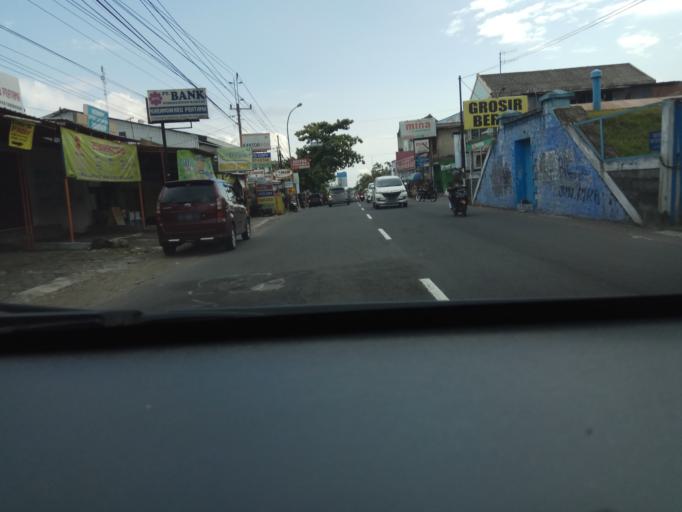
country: ID
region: Daerah Istimewa Yogyakarta
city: Melati
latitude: -7.7185
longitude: 110.4046
